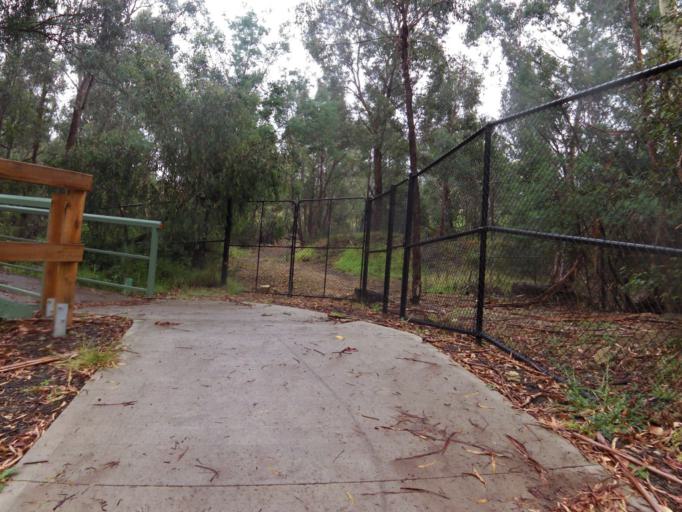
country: AU
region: Victoria
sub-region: Manningham
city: Park Orchards
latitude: -37.7910
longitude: 145.2028
